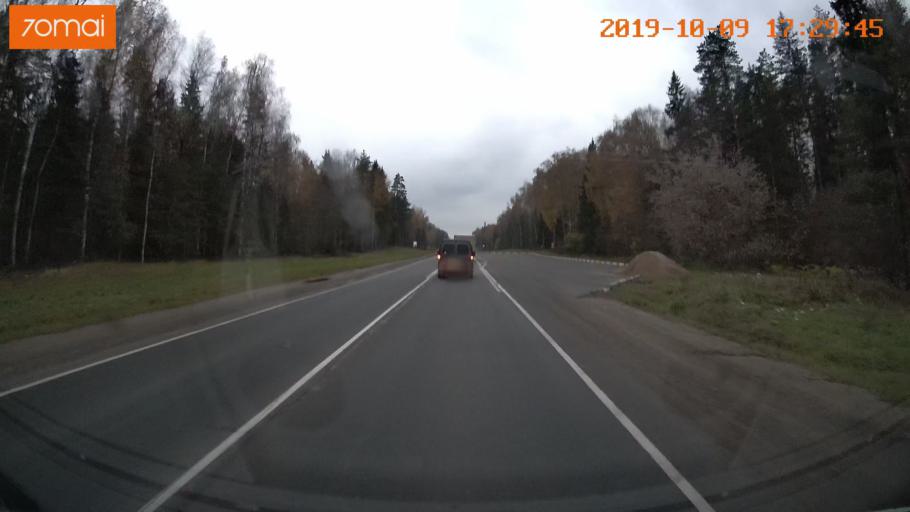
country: RU
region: Ivanovo
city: Bogorodskoye
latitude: 57.1477
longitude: 41.0563
